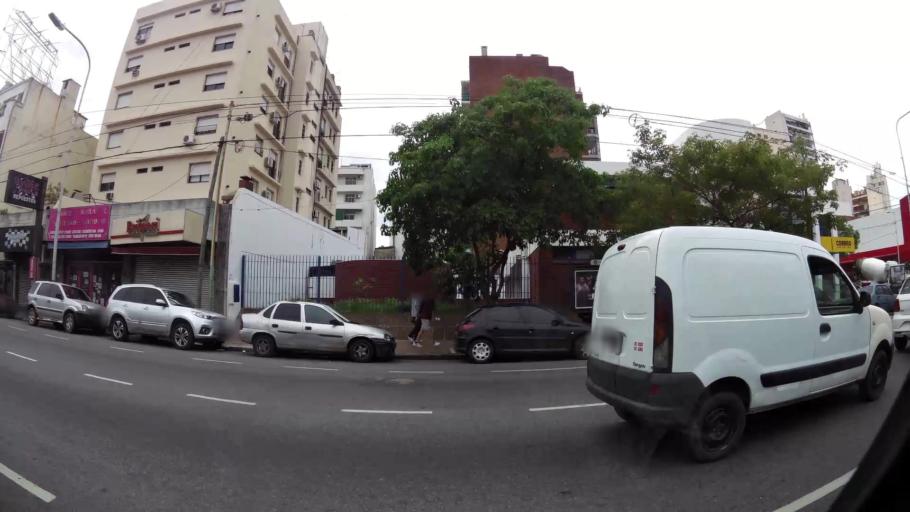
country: AR
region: Buenos Aires
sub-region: Partido de Avellaneda
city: Avellaneda
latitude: -34.6611
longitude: -58.3687
